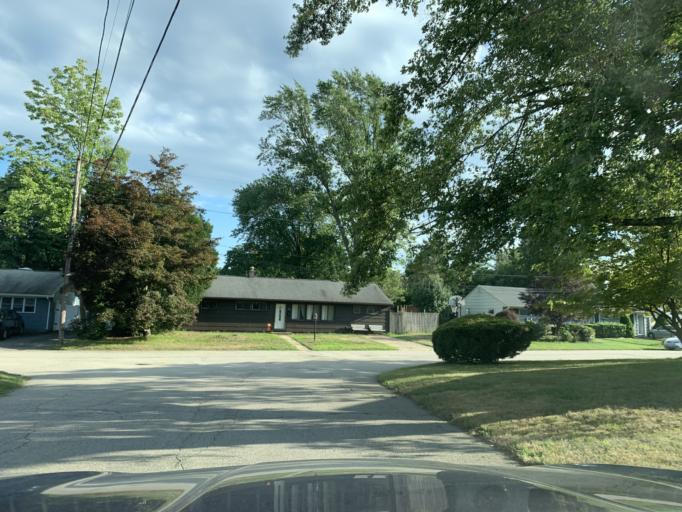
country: US
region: Rhode Island
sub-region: Kent County
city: West Warwick
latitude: 41.6990
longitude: -71.5148
